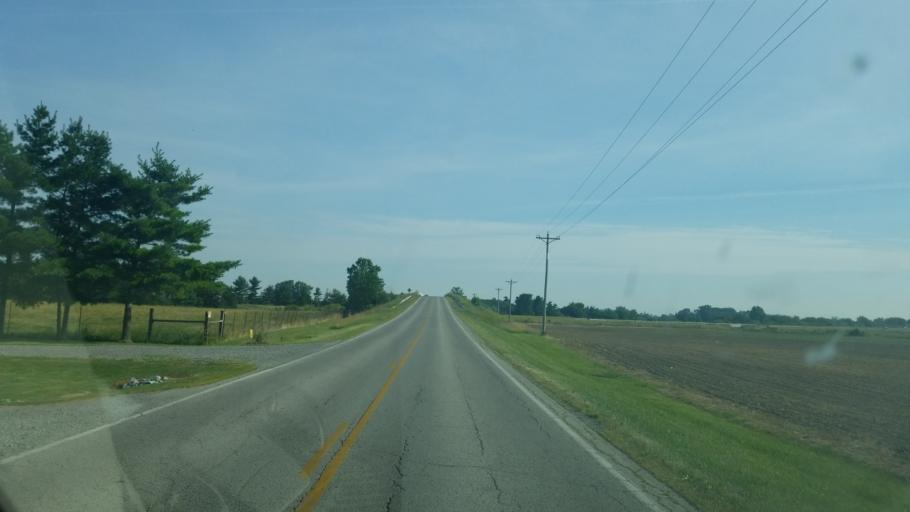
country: US
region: Ohio
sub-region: Hancock County
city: Findlay
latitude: 40.9910
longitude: -83.6985
